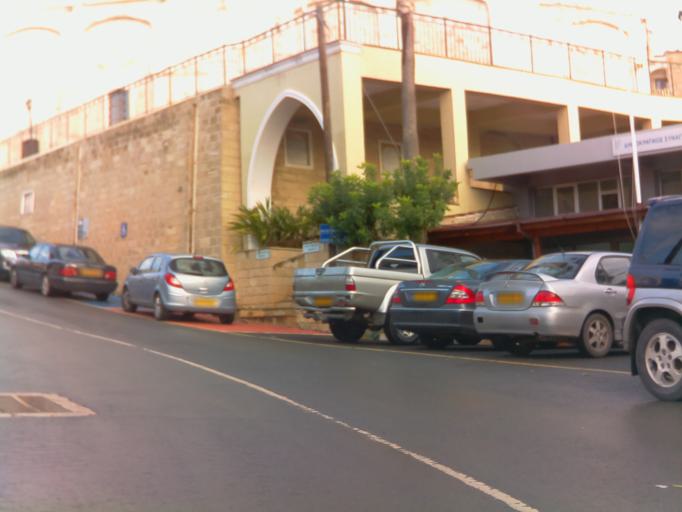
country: CY
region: Pafos
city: Pegeia
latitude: 34.8841
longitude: 32.3820
